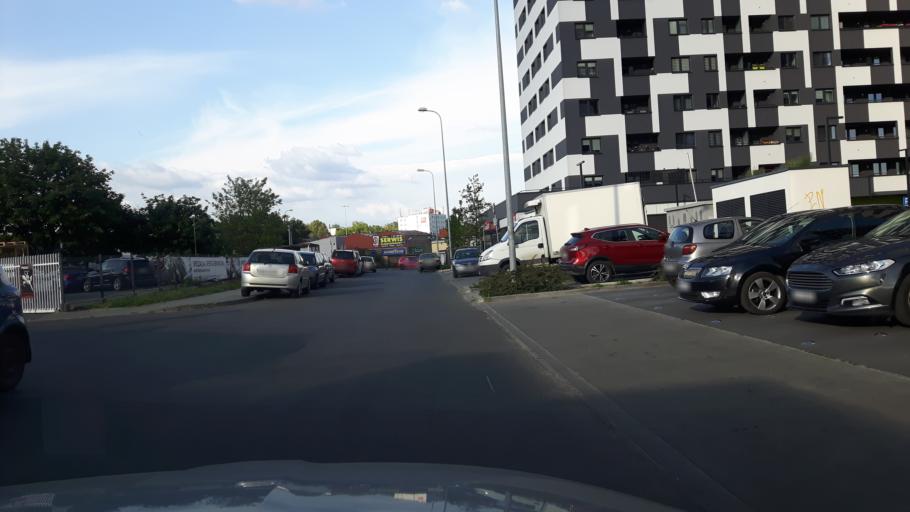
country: PL
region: Masovian Voivodeship
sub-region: Warszawa
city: Praga Poludnie
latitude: 52.2316
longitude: 21.1142
